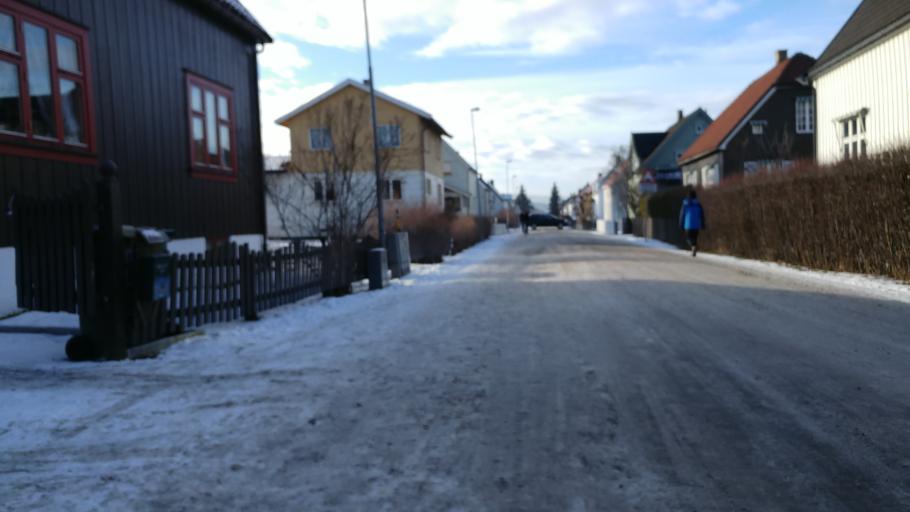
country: NO
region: Akershus
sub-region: Skedsmo
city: Lillestrom
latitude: 59.9588
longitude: 11.0467
